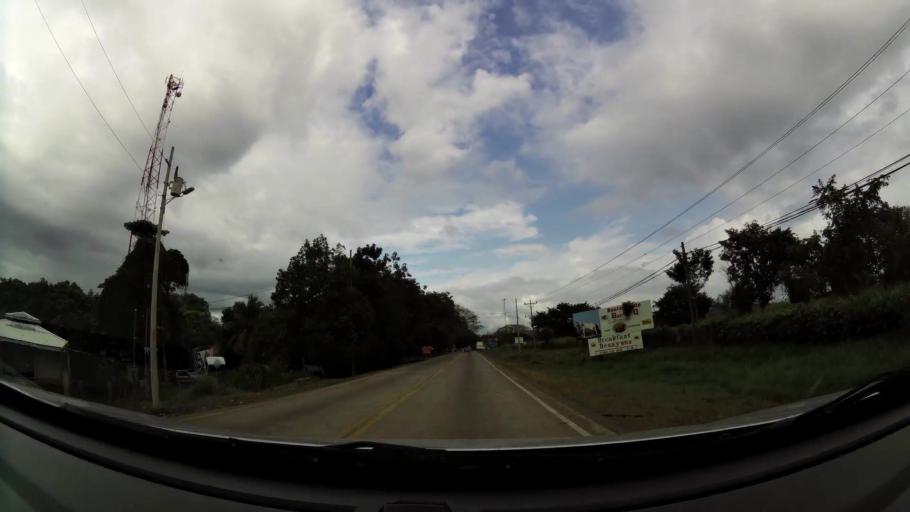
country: CR
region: Guanacaste
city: Juntas
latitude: 10.2648
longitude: -85.0242
